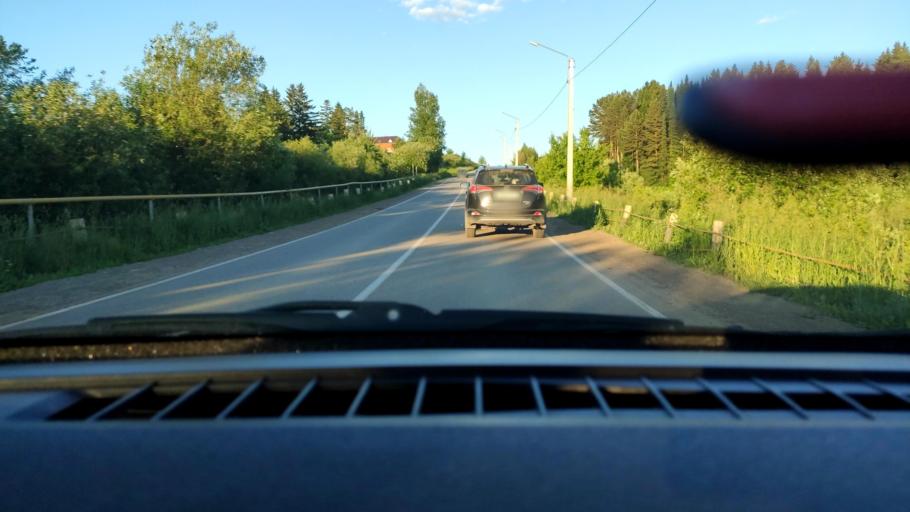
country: RU
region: Perm
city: Kultayevo
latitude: 57.9250
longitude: 55.8985
